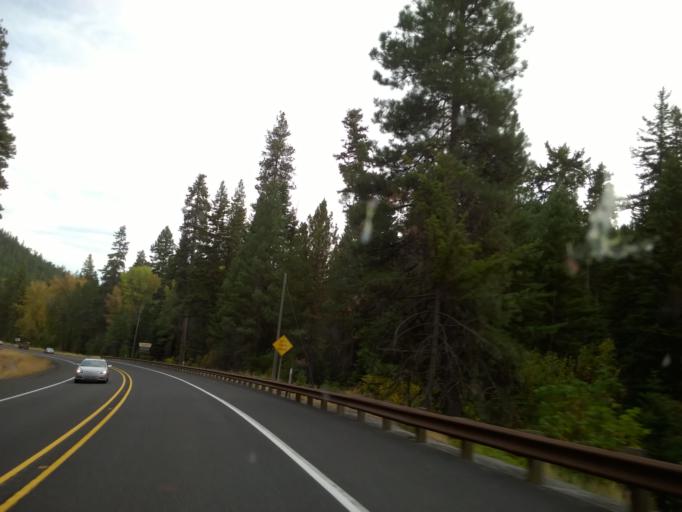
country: US
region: Washington
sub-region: Kittitas County
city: Cle Elum
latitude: 47.2919
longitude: -120.7004
